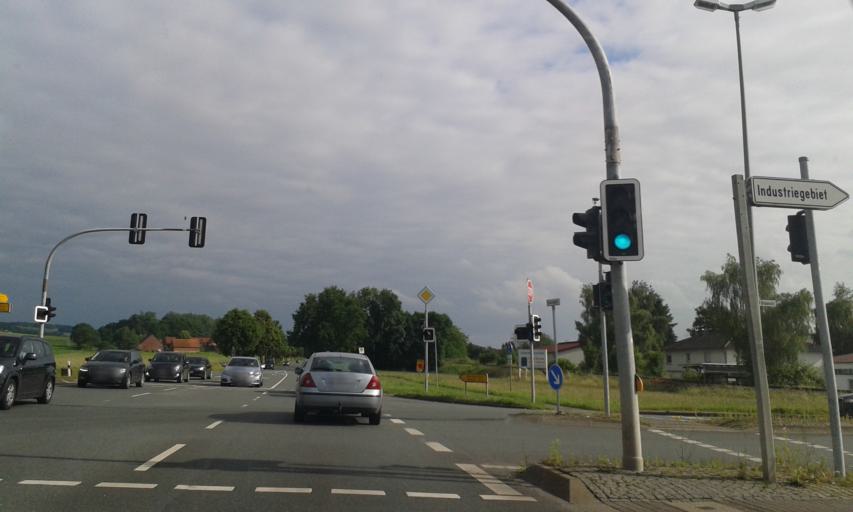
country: DE
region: Lower Saxony
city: Rinteln
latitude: 52.1690
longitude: 9.0851
